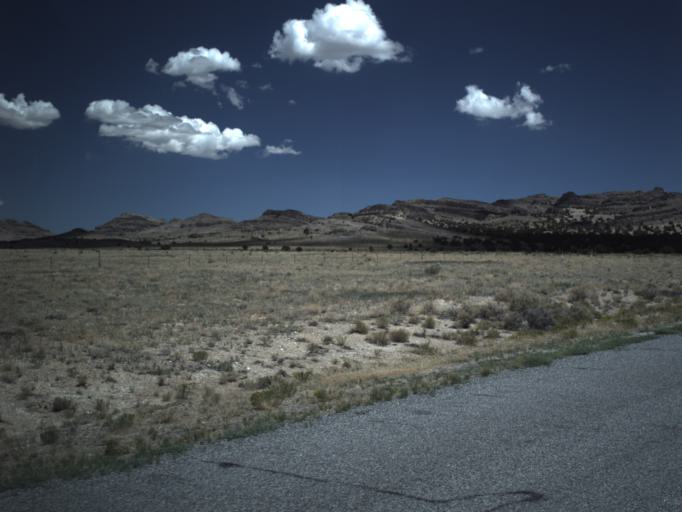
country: US
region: Utah
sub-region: Beaver County
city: Milford
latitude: 39.0694
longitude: -113.7307
